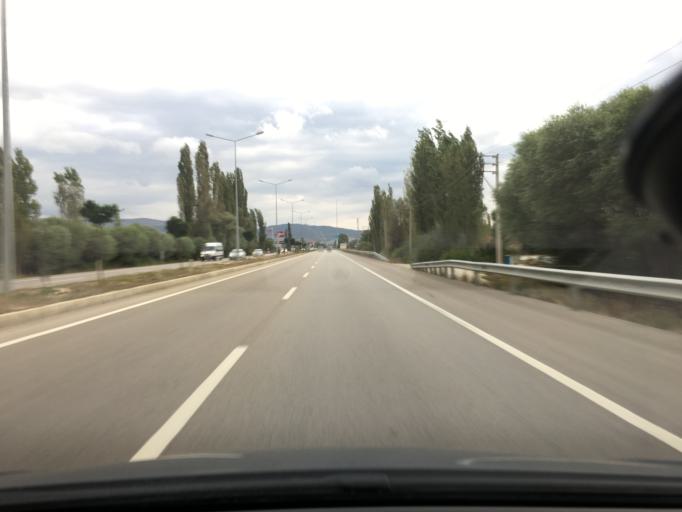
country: TR
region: Afyonkarahisar
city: Sincanli
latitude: 38.7657
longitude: 30.3660
